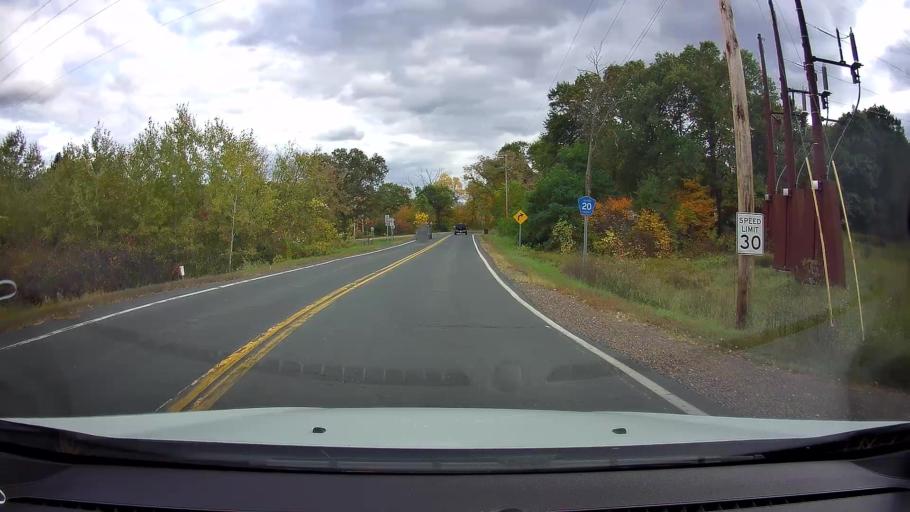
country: US
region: Wisconsin
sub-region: Polk County
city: Saint Croix Falls
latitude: 45.4119
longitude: -92.6619
